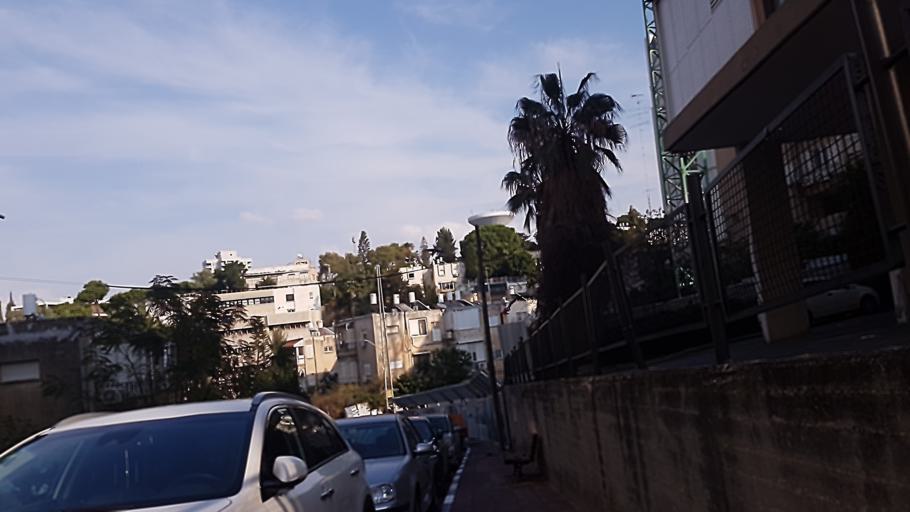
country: IL
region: Tel Aviv
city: Ramat Gan
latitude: 32.0825
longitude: 34.8086
